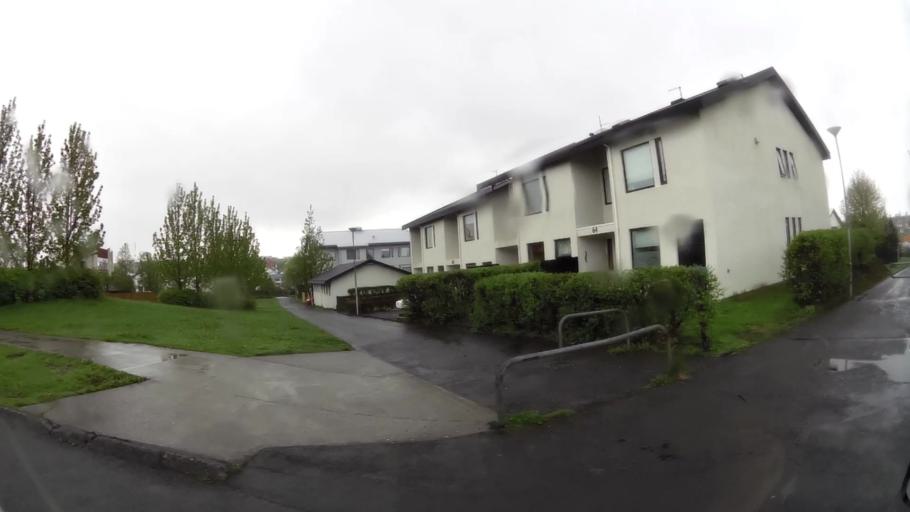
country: IS
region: Capital Region
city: Reykjavik
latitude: 64.0967
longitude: -21.8354
